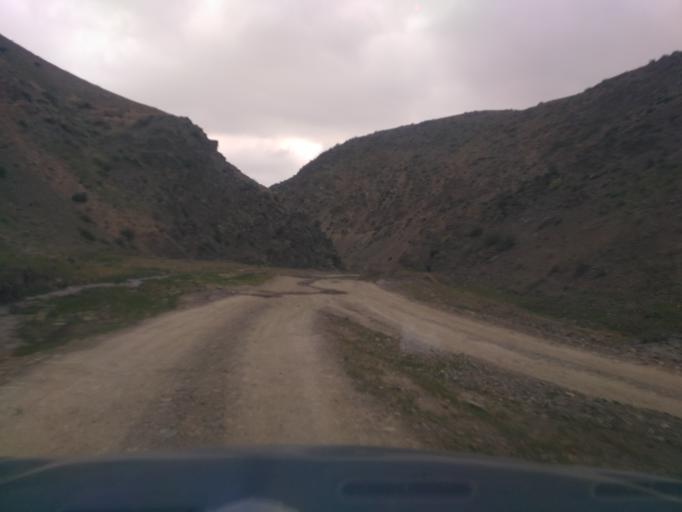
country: UZ
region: Jizzax
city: Zomin
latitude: 39.8531
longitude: 68.3931
